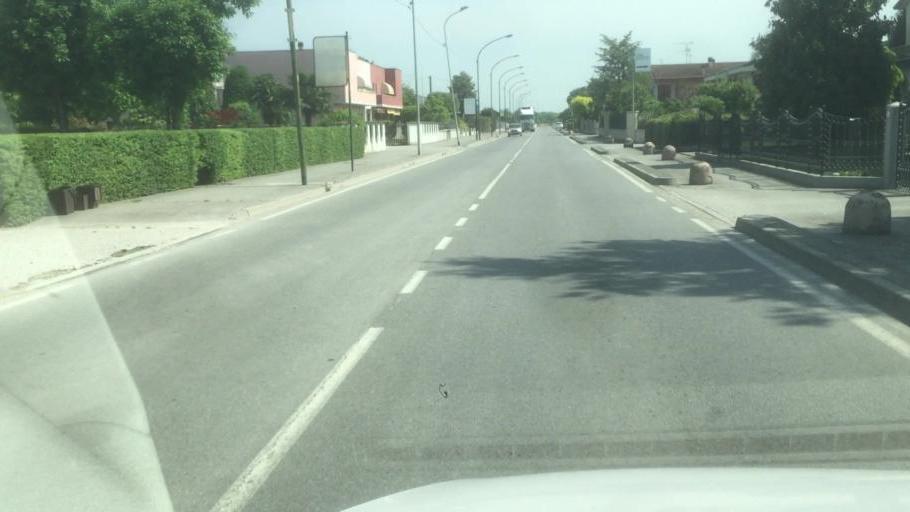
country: IT
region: Lombardy
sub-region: Provincia di Mantova
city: Casaloldo
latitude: 45.2474
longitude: 10.4573
